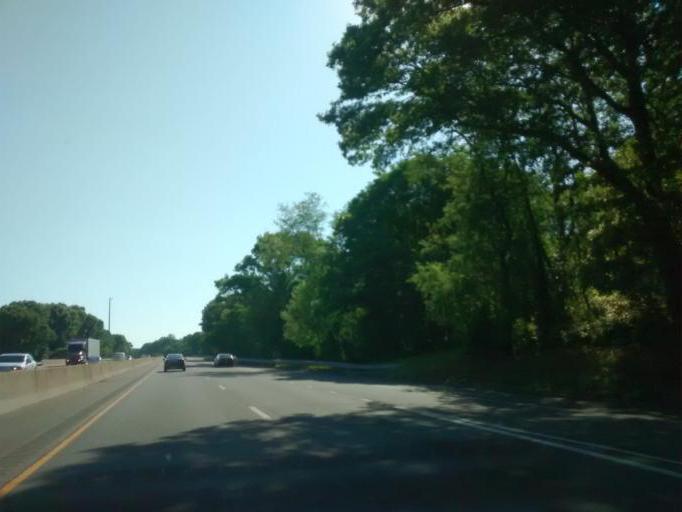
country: US
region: Connecticut
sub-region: Middlesex County
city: Old Saybrook
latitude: 41.3057
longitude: -72.3786
